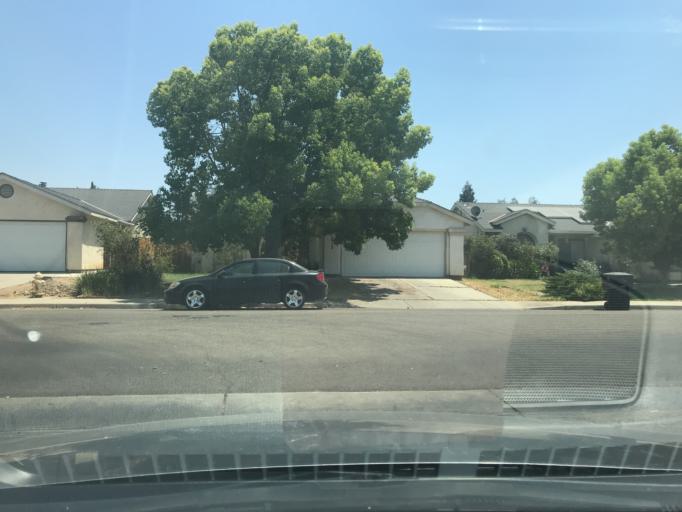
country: US
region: California
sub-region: Merced County
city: Atwater
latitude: 37.3634
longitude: -120.6008
